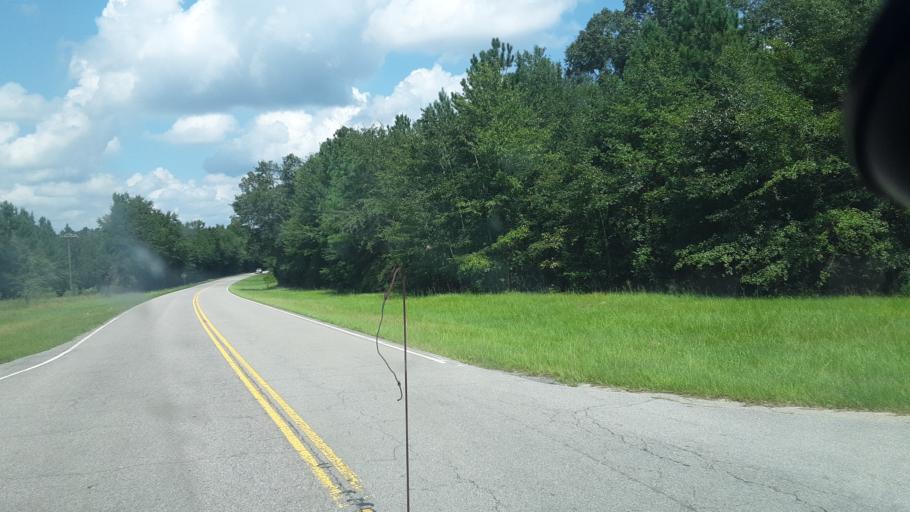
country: US
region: South Carolina
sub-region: Calhoun County
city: Oak Grove
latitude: 33.7121
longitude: -80.9531
